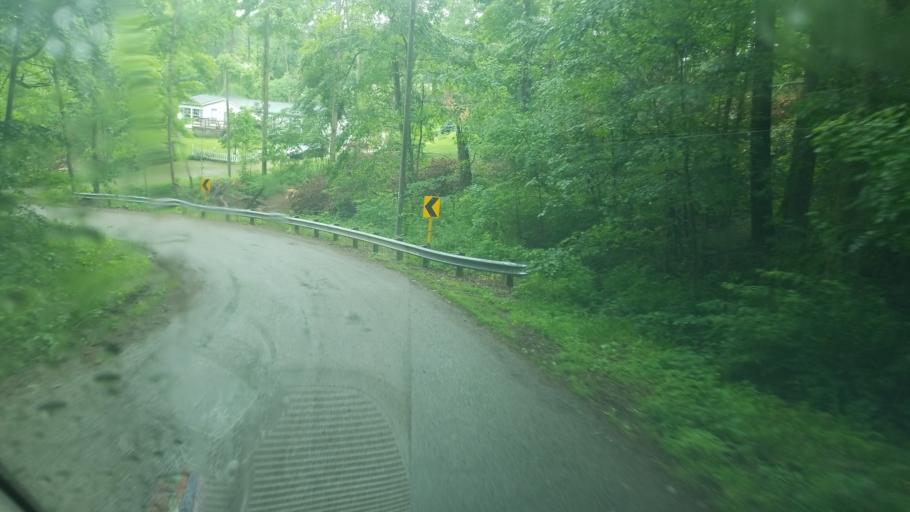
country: US
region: Ohio
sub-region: Sandusky County
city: Bellville
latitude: 40.6170
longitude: -82.4633
